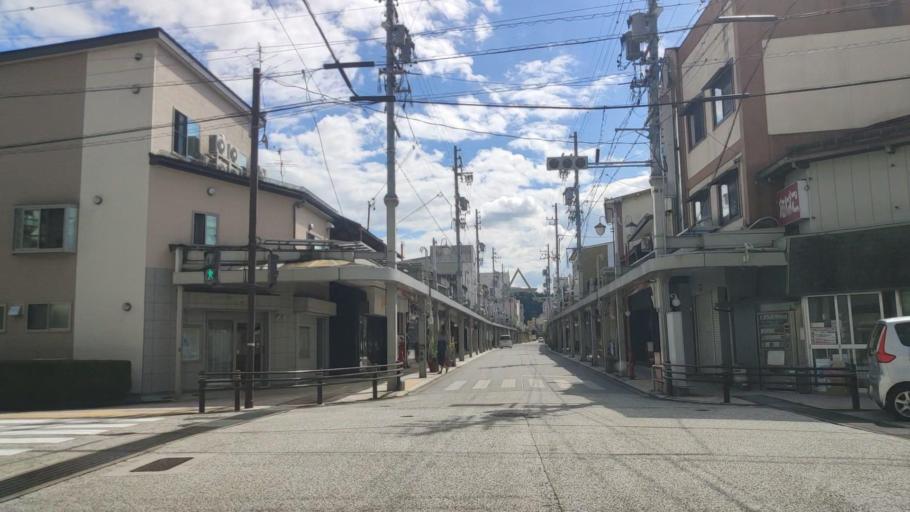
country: JP
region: Gifu
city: Takayama
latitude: 36.1463
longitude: 137.2566
